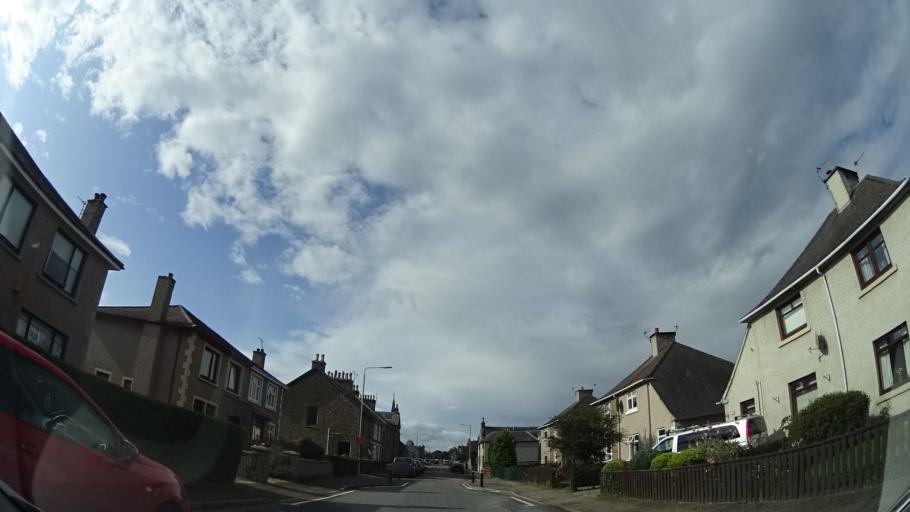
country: GB
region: Scotland
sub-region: Highland
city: Inverness
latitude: 57.4828
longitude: -4.2373
